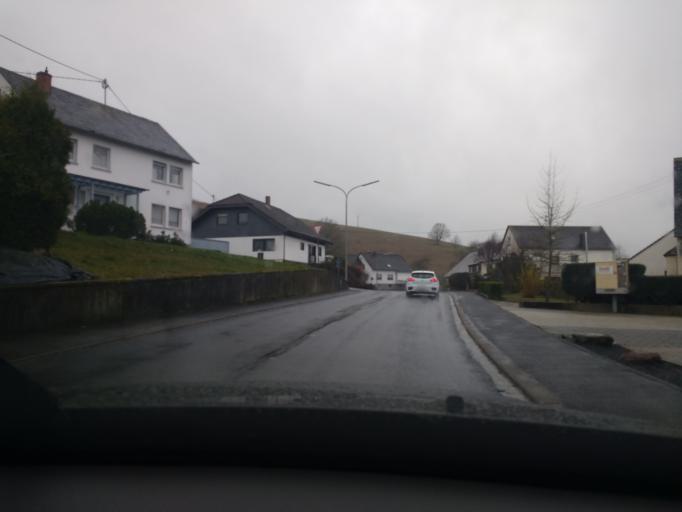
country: DE
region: Rheinland-Pfalz
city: Pluwig
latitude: 49.6871
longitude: 6.7189
